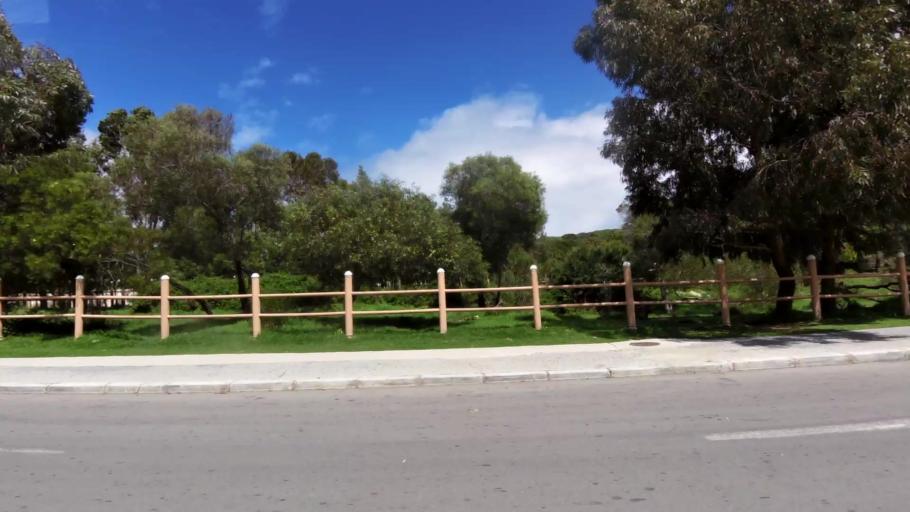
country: MA
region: Tanger-Tetouan
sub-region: Tanger-Assilah
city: Boukhalef
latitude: 35.7857
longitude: -5.8660
